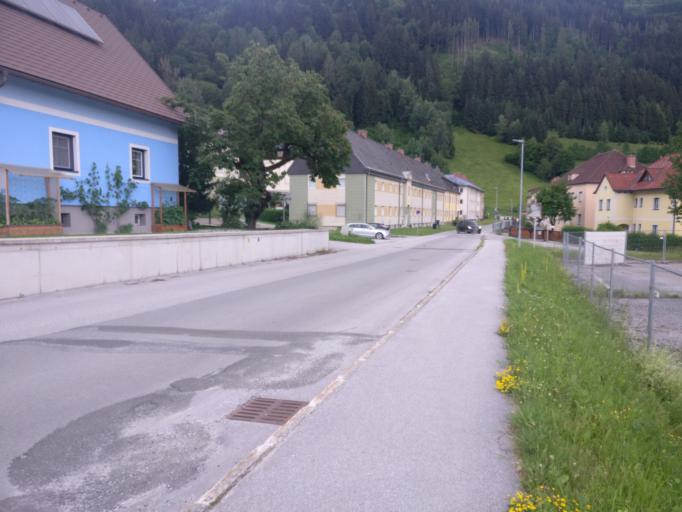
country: AT
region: Styria
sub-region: Politischer Bezirk Liezen
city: Selzthal
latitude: 47.5558
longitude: 14.3219
